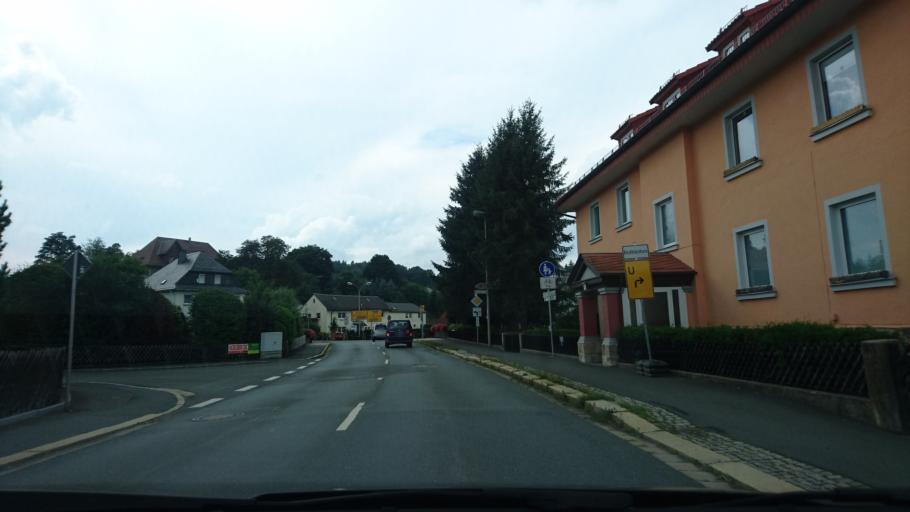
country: DE
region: Bavaria
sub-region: Upper Franconia
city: Lichtenberg
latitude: 50.3563
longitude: 11.6846
